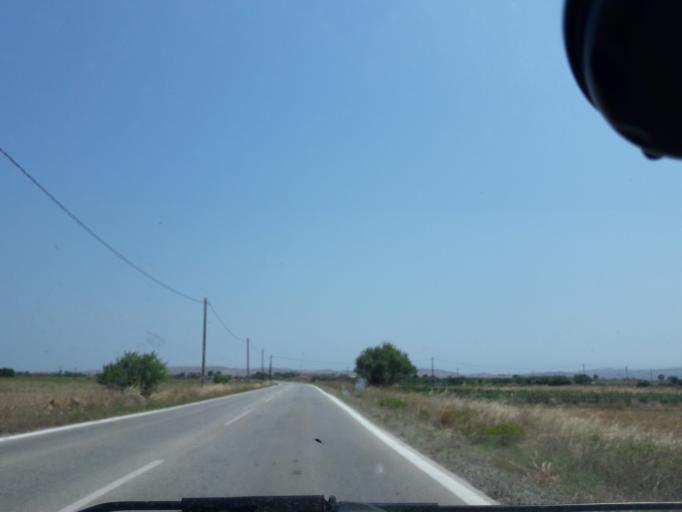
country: GR
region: North Aegean
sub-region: Nomos Lesvou
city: Myrina
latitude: 39.9132
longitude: 25.2099
